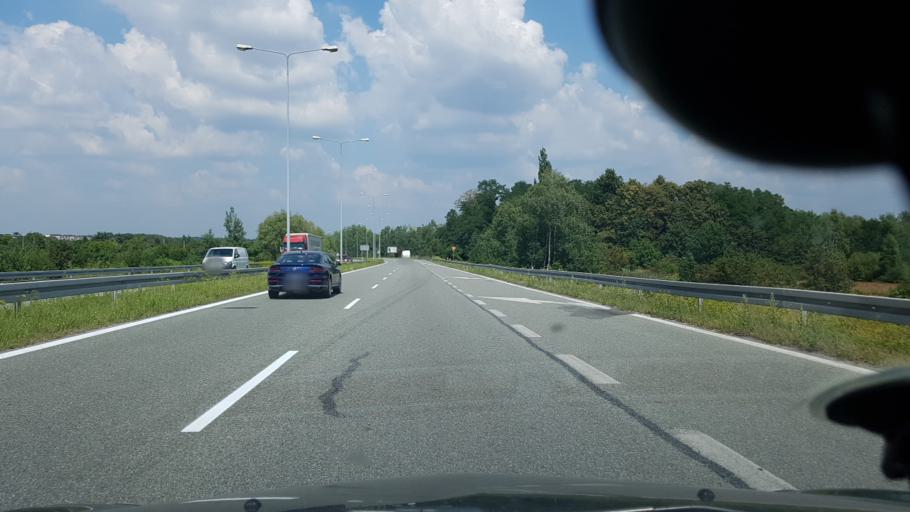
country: PL
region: Silesian Voivodeship
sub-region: Powiat mikolowski
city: Laziska Gorne
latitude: 50.1501
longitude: 18.8503
